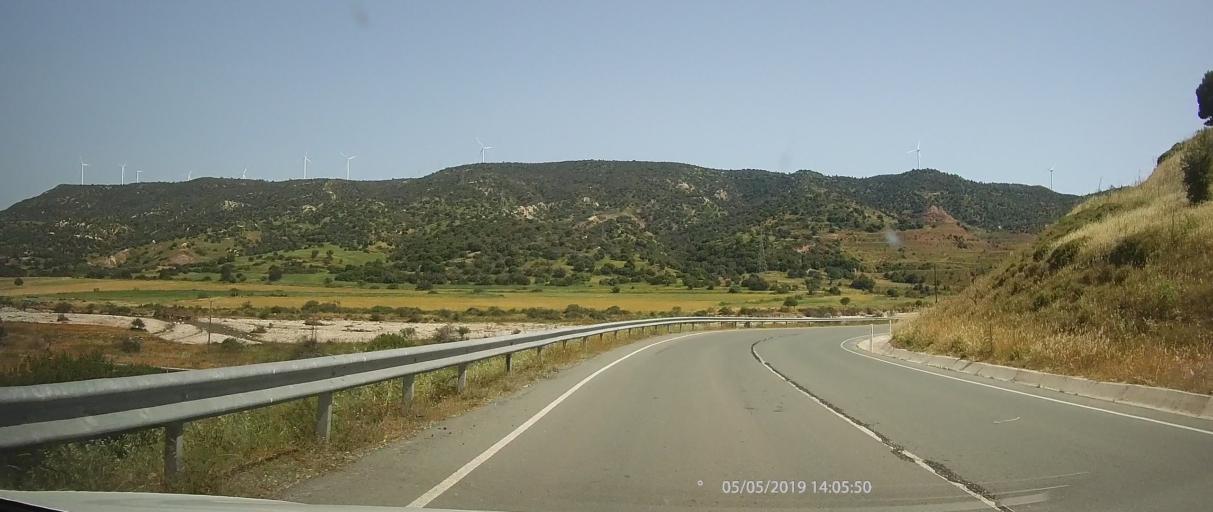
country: CY
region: Limassol
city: Pissouri
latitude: 34.7490
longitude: 32.6094
